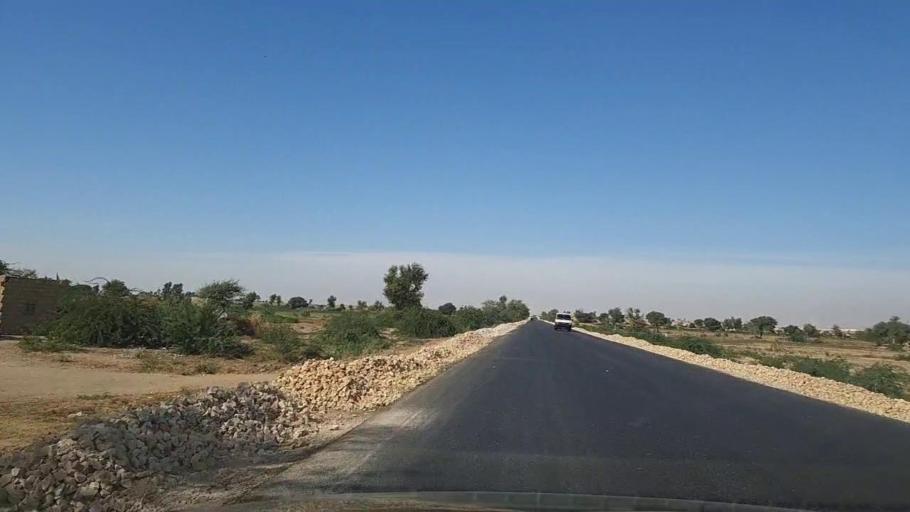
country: PK
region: Sindh
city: Kotri
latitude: 25.2863
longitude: 68.2088
